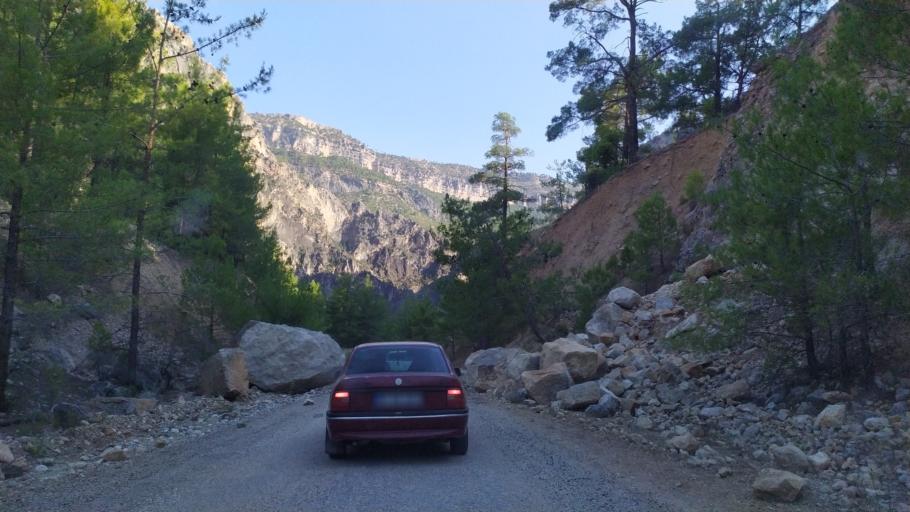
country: TR
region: Mersin
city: Mut
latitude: 36.5460
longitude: 33.2334
